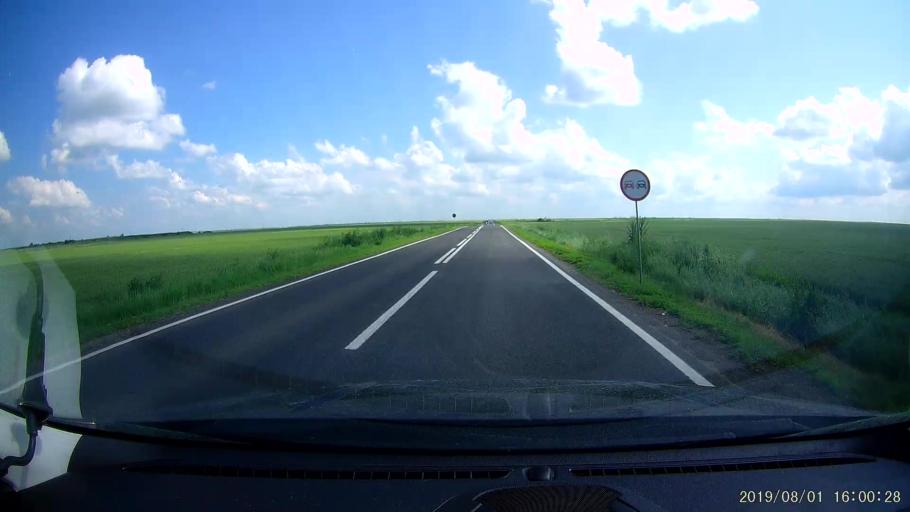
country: RO
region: Ialomita
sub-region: Comuna Ciulnita
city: Ciulnita
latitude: 44.5290
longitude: 27.3888
